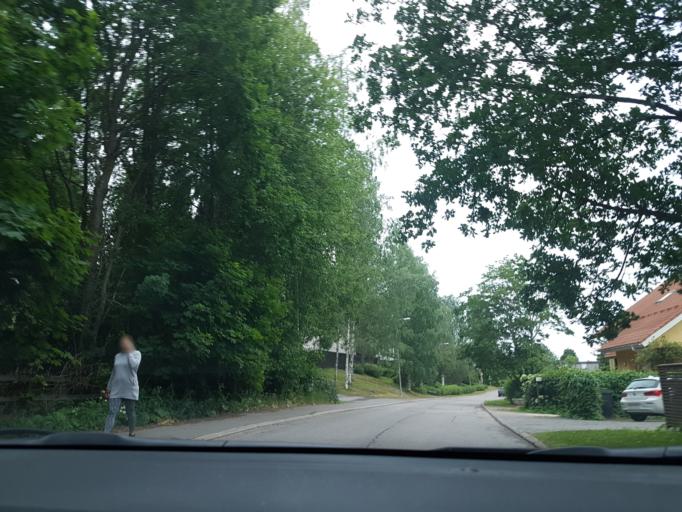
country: FI
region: Uusimaa
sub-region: Helsinki
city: Vantaa
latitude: 60.2212
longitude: 25.1293
